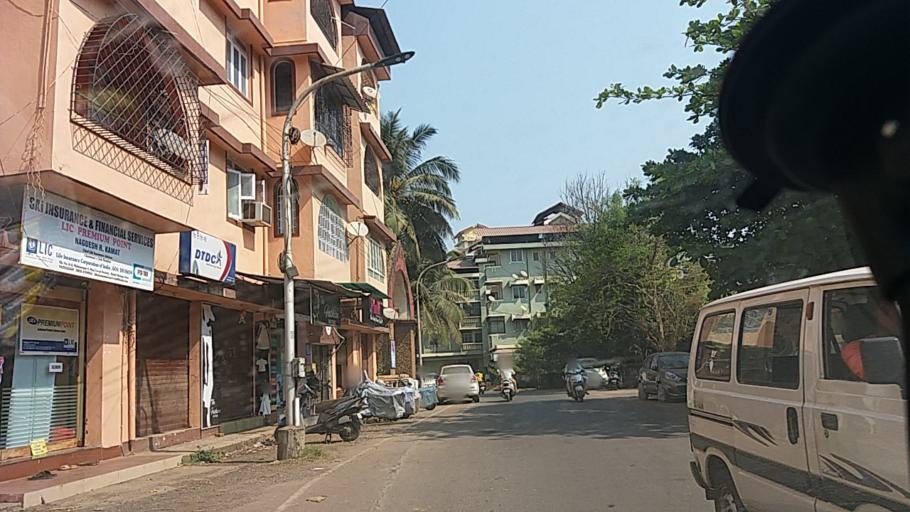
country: IN
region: Goa
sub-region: South Goa
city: Madgaon
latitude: 15.2868
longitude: 73.9534
